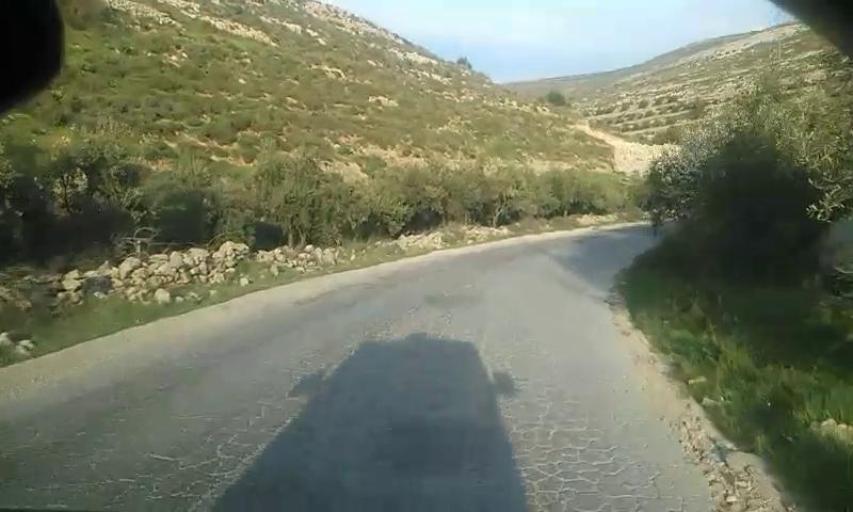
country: PS
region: West Bank
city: Marah Rabbah
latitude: 31.5998
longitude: 35.1820
